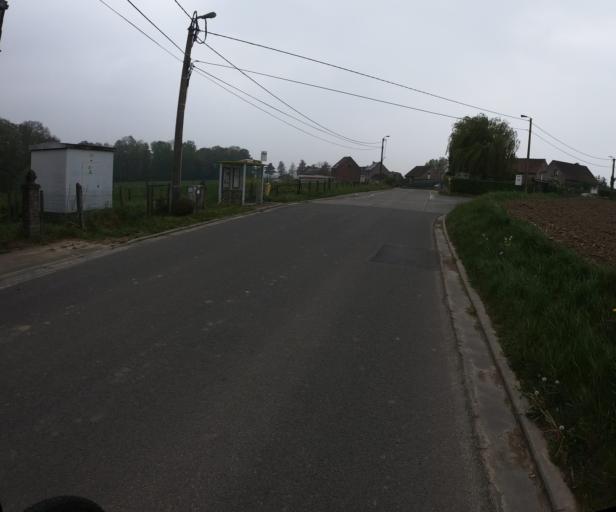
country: BE
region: Flanders
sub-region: Provincie Vlaams-Brabant
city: Pepingen
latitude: 50.7285
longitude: 4.1570
